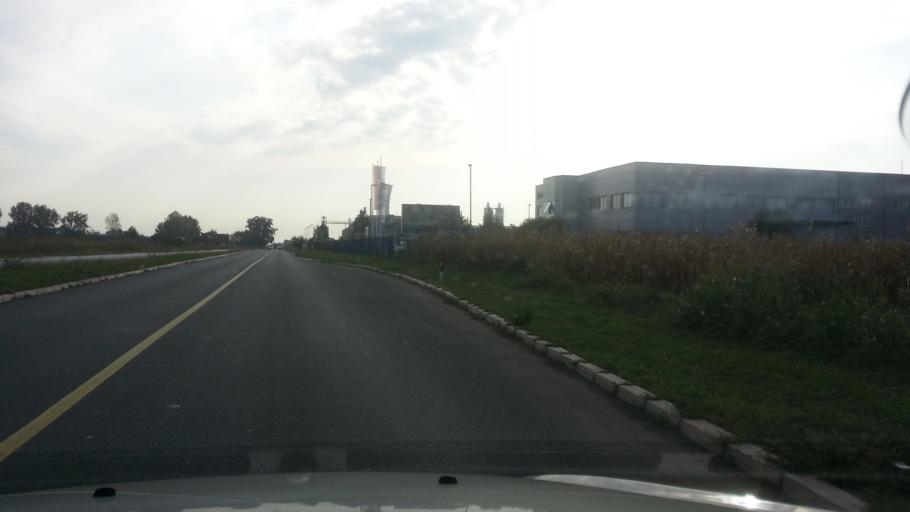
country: RS
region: Autonomna Pokrajina Vojvodina
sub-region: Sremski Okrug
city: Stara Pazova
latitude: 44.9866
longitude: 20.1985
